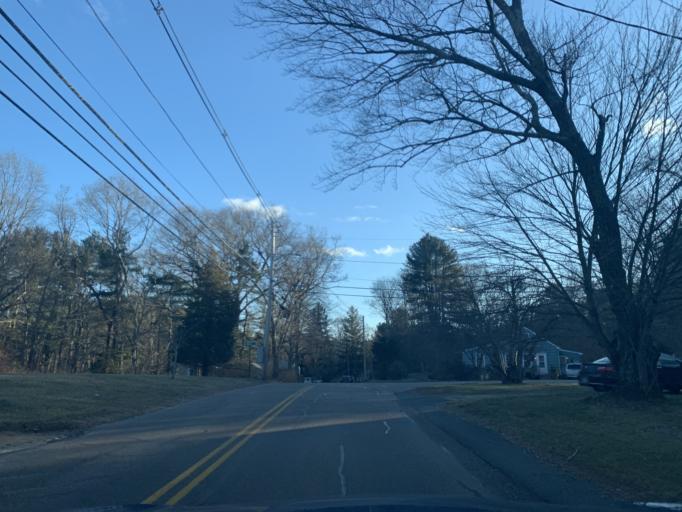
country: US
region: Massachusetts
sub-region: Bristol County
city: Norton
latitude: 41.9411
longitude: -71.2024
